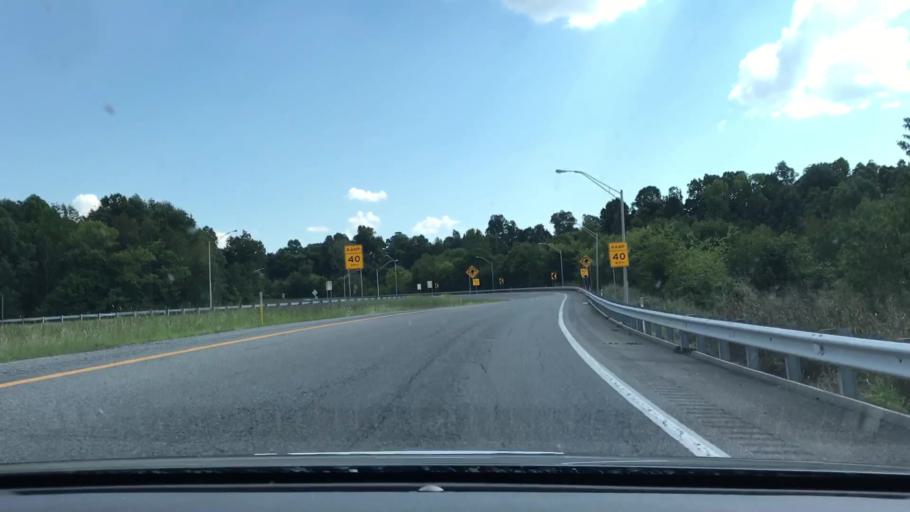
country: US
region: Kentucky
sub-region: Lyon County
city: Eddyville
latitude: 37.0716
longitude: -88.0900
